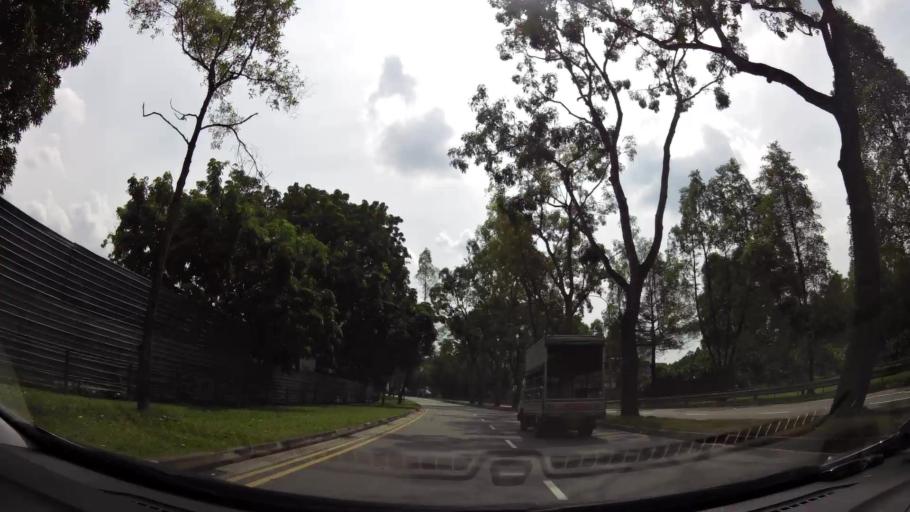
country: MY
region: Johor
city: Johor Bahru
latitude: 1.4217
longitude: 103.7433
